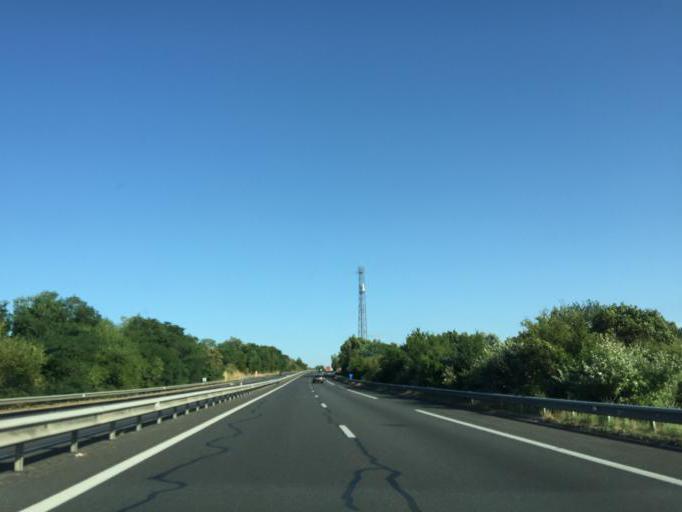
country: FR
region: Auvergne
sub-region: Departement de l'Allier
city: Doyet
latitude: 46.3435
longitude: 2.8749
